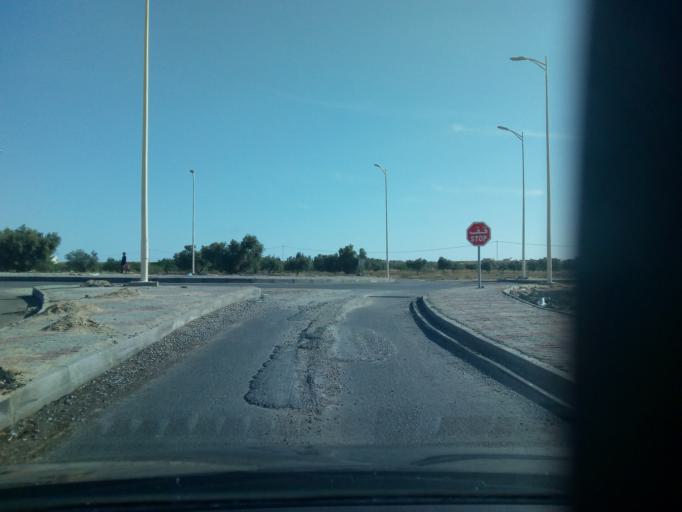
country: TN
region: Safaqis
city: Sfax
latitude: 34.7282
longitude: 10.6157
